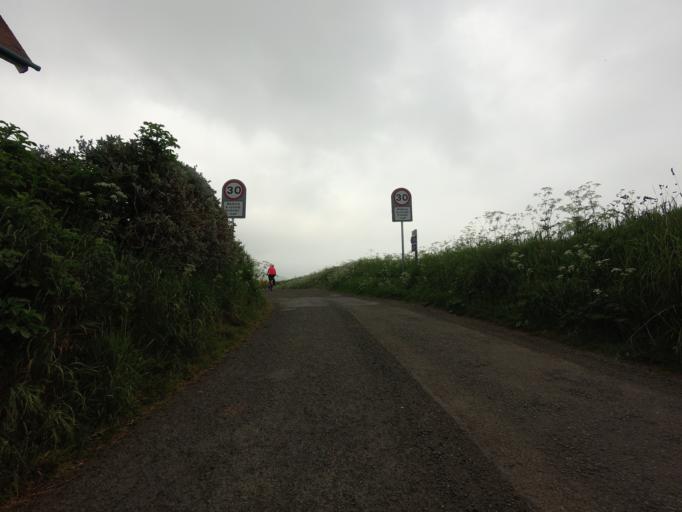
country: GB
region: Scotland
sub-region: Fife
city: Ballingry
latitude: 56.2292
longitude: -3.3425
